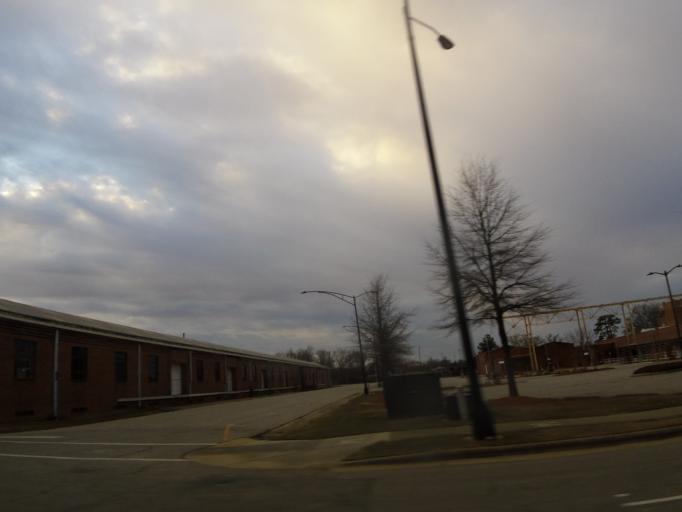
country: US
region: North Carolina
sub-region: Nash County
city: Rocky Mount
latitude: 35.9459
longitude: -77.7957
